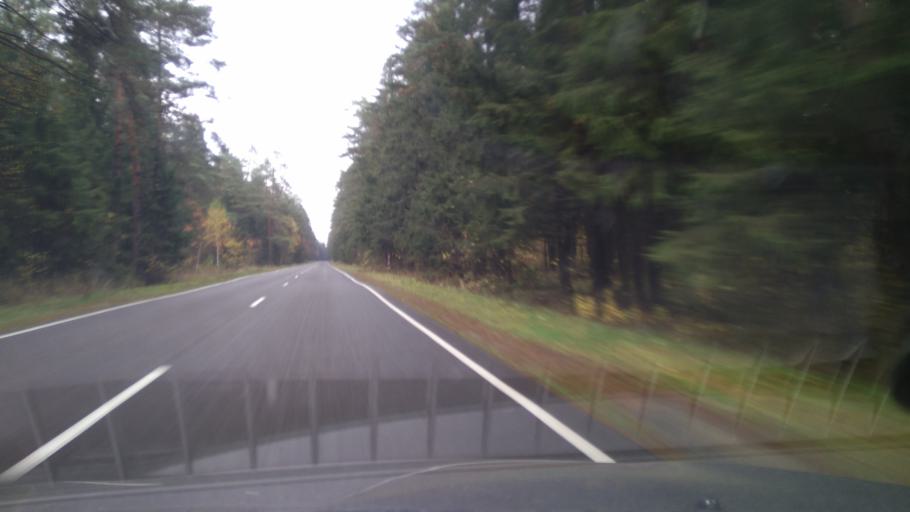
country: BY
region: Minsk
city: Slutsk
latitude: 53.2253
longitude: 27.6100
